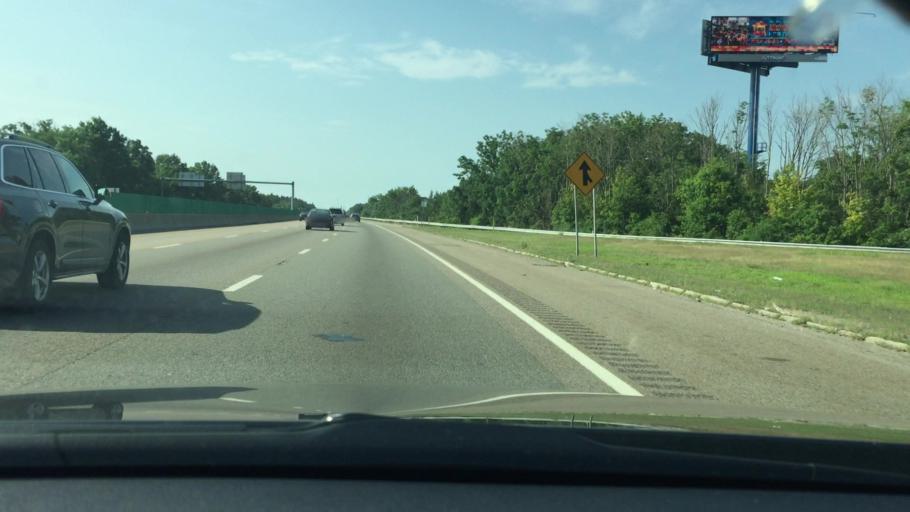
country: US
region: Massachusetts
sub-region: Plymouth County
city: Brockton
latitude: 42.0602
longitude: -71.0618
